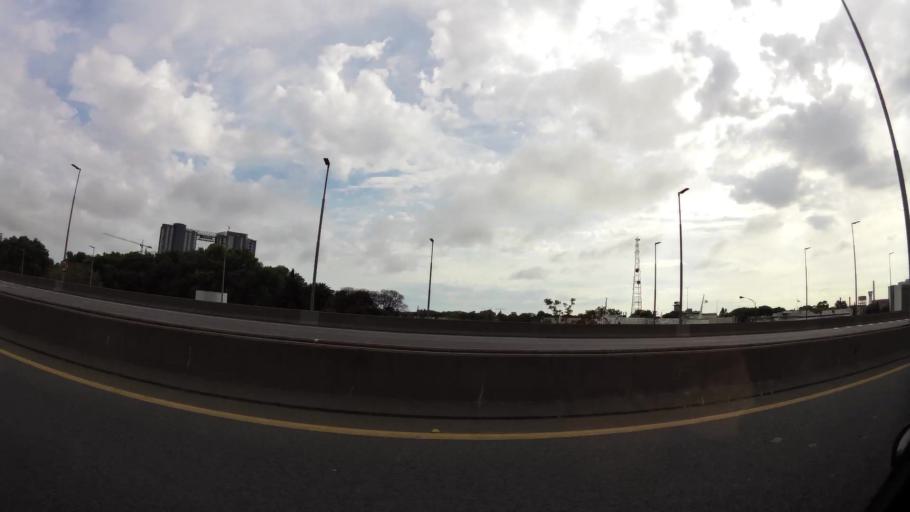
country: AR
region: Buenos Aires F.D.
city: Buenos Aires
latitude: -34.6247
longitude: -58.3613
